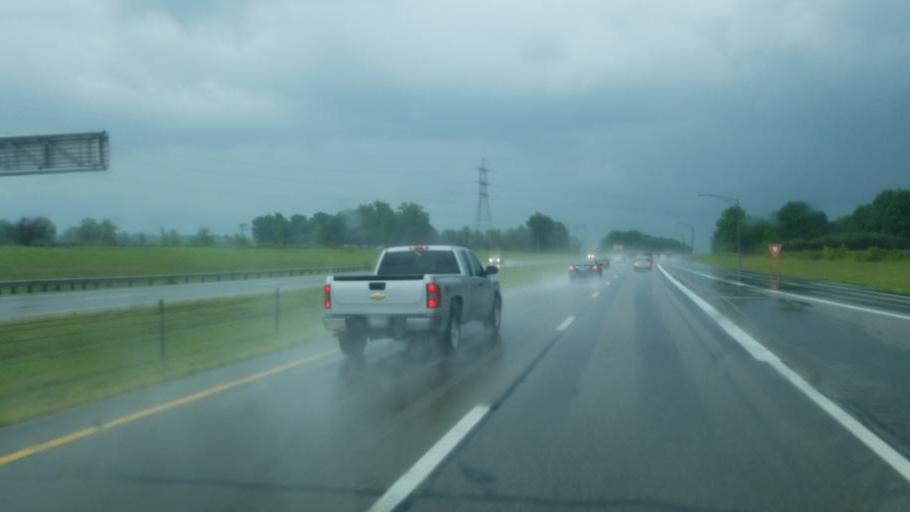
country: US
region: Ohio
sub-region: Trumbull County
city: Morgandale
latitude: 41.2771
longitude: -80.7986
